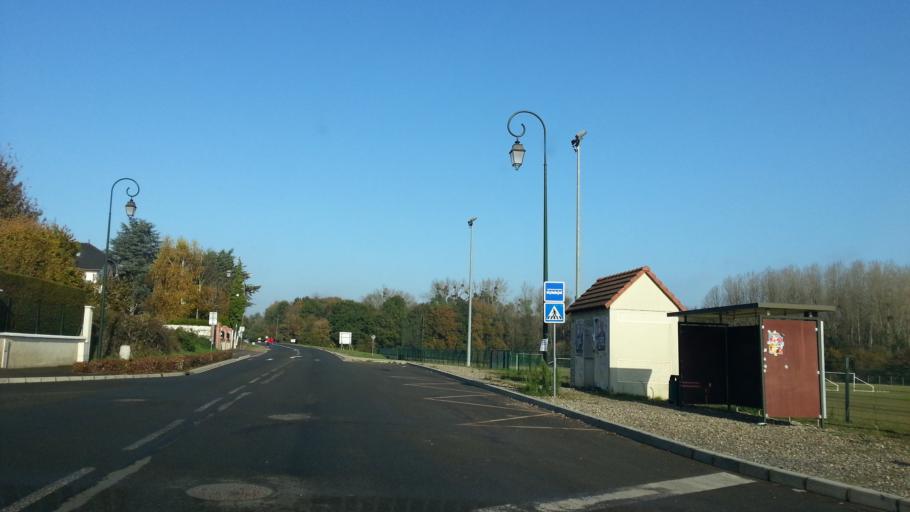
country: FR
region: Picardie
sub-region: Departement de l'Oise
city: Balagny-sur-Therain
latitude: 49.3009
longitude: 2.3323
